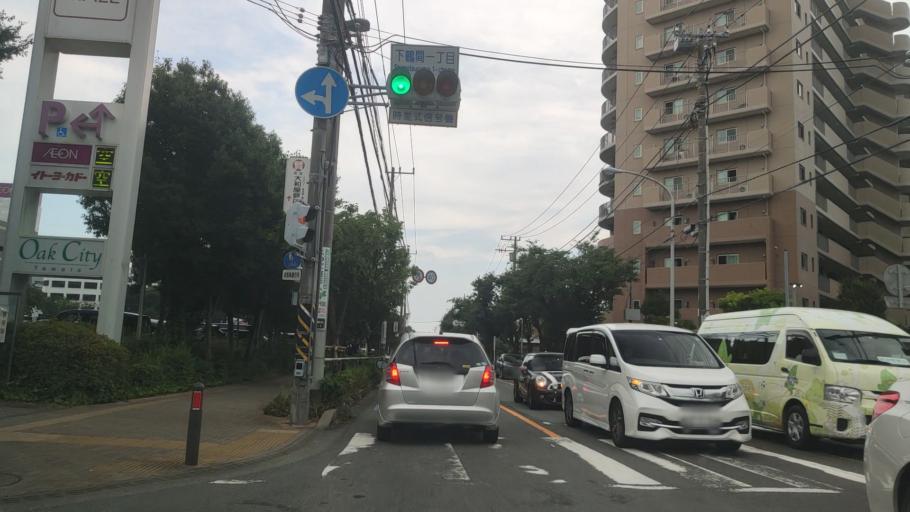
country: JP
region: Kanagawa
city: Minami-rinkan
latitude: 35.4893
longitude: 139.4562
